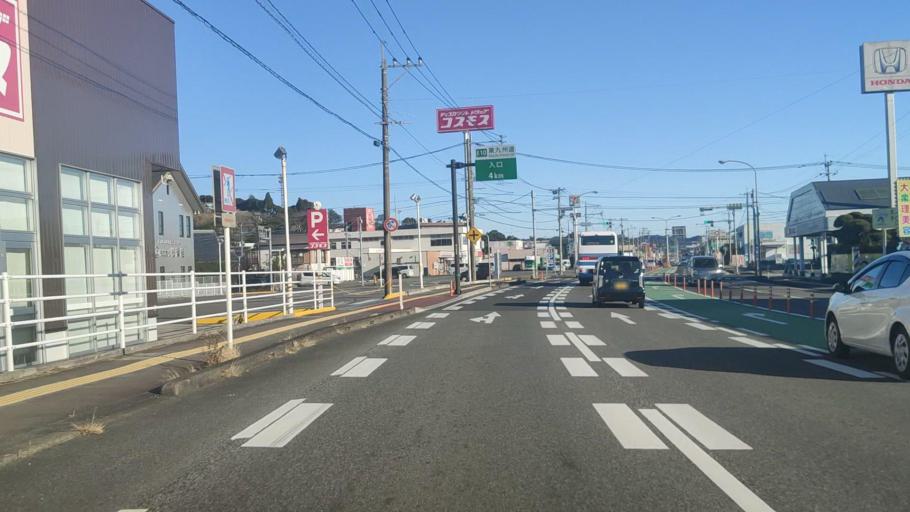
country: JP
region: Miyazaki
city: Nobeoka
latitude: 32.4672
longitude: 131.6481
